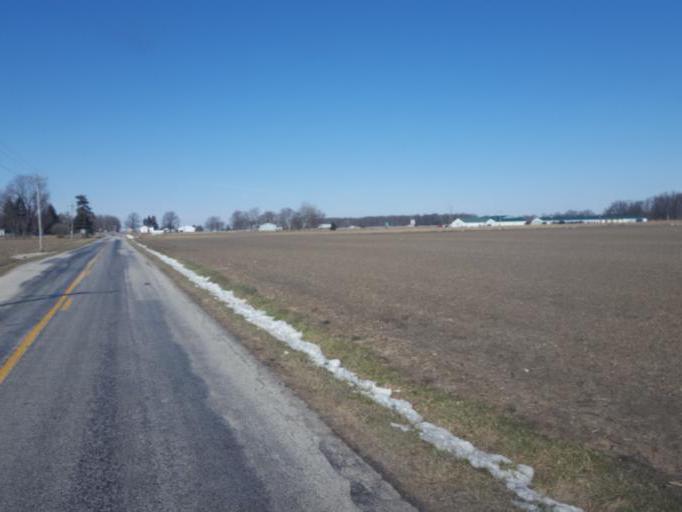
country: US
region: Ohio
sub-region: Marion County
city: Marion
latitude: 40.6520
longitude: -83.0998
